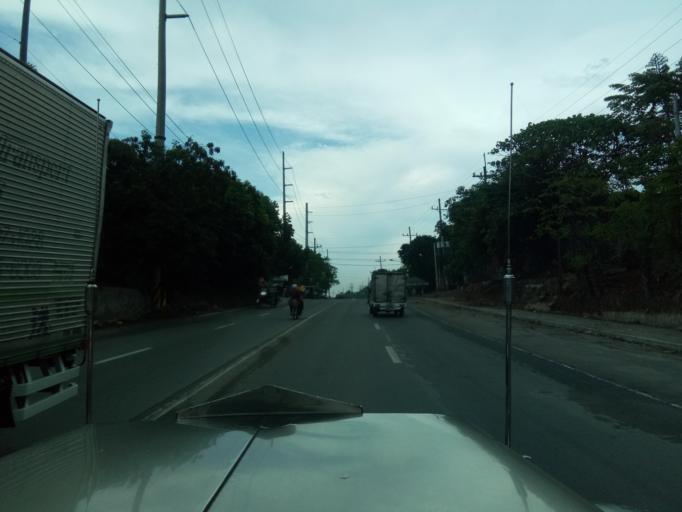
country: PH
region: Calabarzon
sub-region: Province of Cavite
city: Aliang
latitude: 14.2801
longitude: 120.8734
